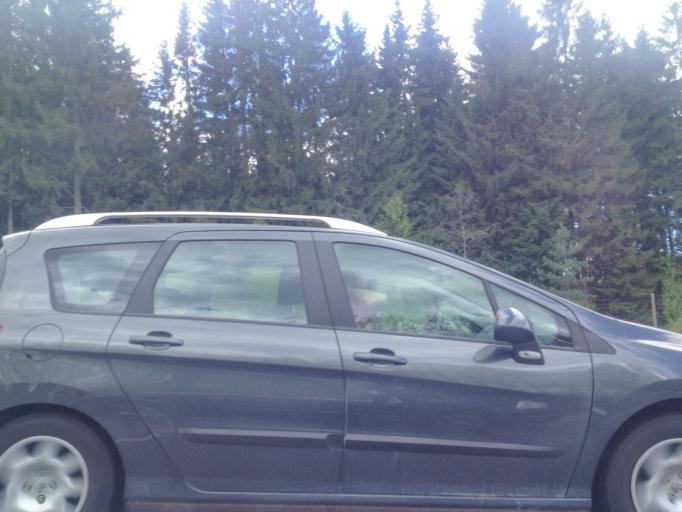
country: FI
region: Haeme
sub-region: Haemeenlinna
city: Haemeenlinna
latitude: 60.9606
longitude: 24.4823
